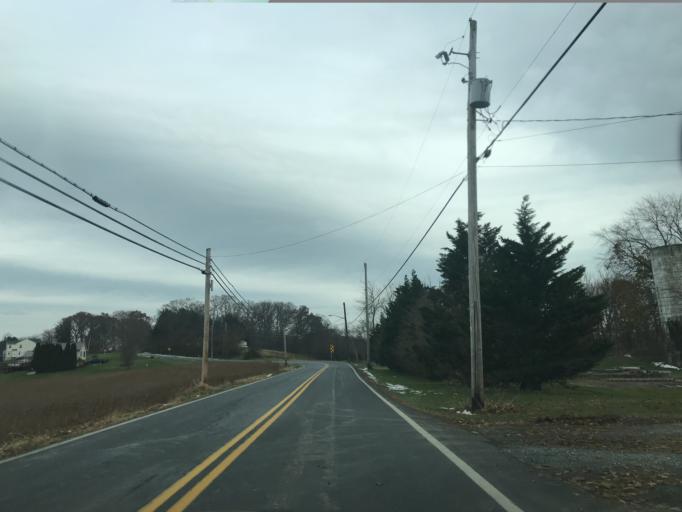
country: US
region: Pennsylvania
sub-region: York County
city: Susquehanna Trails
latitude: 39.6892
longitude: -76.3836
